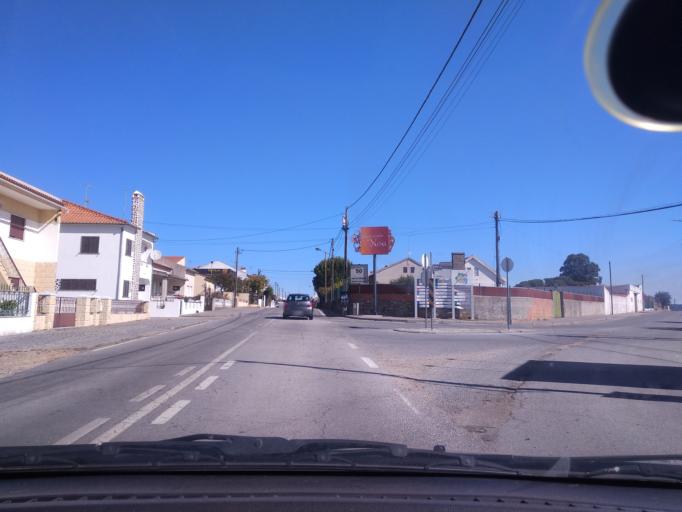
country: PT
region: Portalegre
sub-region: Nisa
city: Nisa
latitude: 39.5074
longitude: -7.6446
